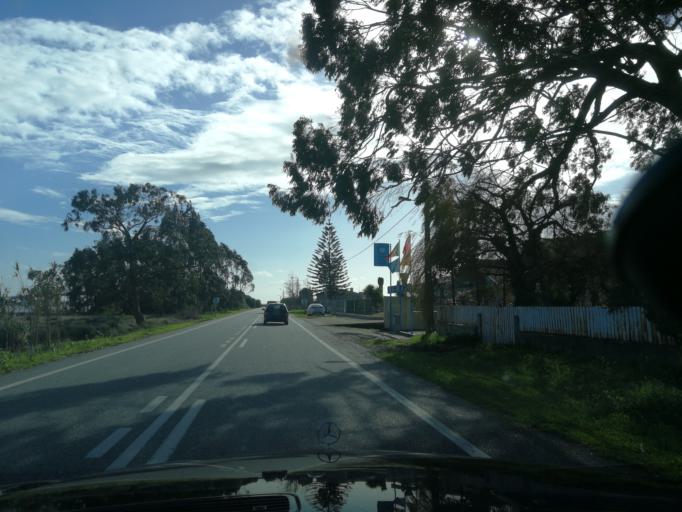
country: PT
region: Aveiro
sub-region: Estarreja
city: Pardilho
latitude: 40.7953
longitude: -8.6736
